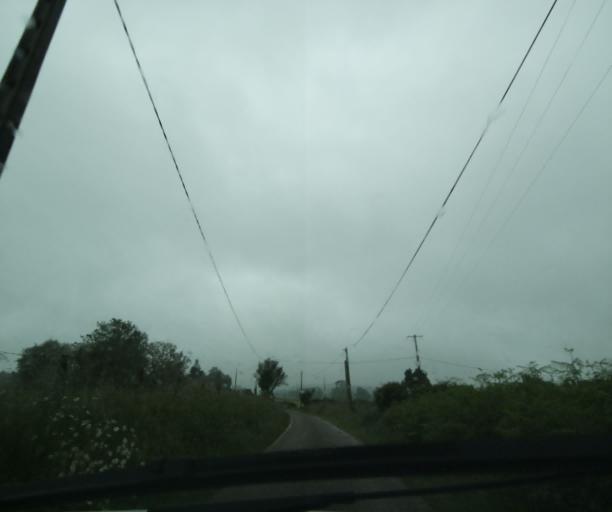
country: FR
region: Bourgogne
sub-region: Departement de Saone-et-Loire
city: Charolles
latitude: 46.3746
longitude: 4.3466
